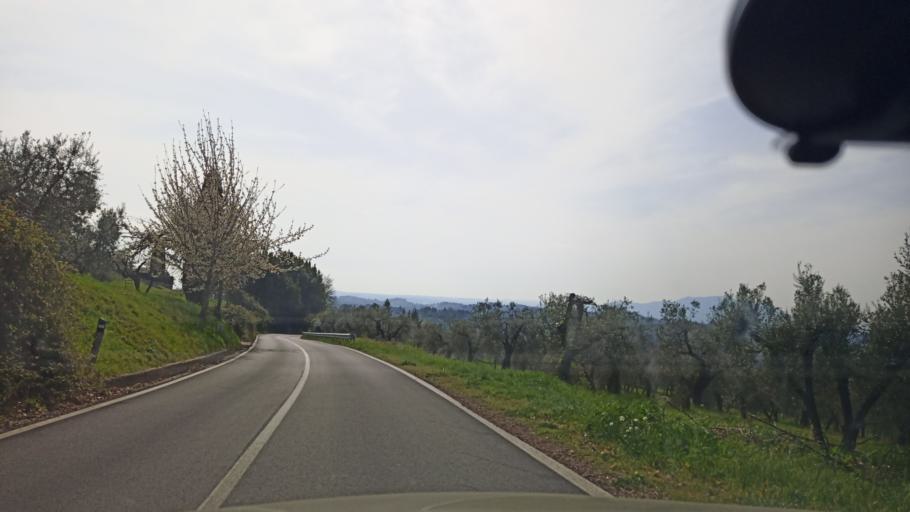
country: IT
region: Latium
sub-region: Provincia di Rieti
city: Torri in Sabina
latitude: 42.3353
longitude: 12.6459
